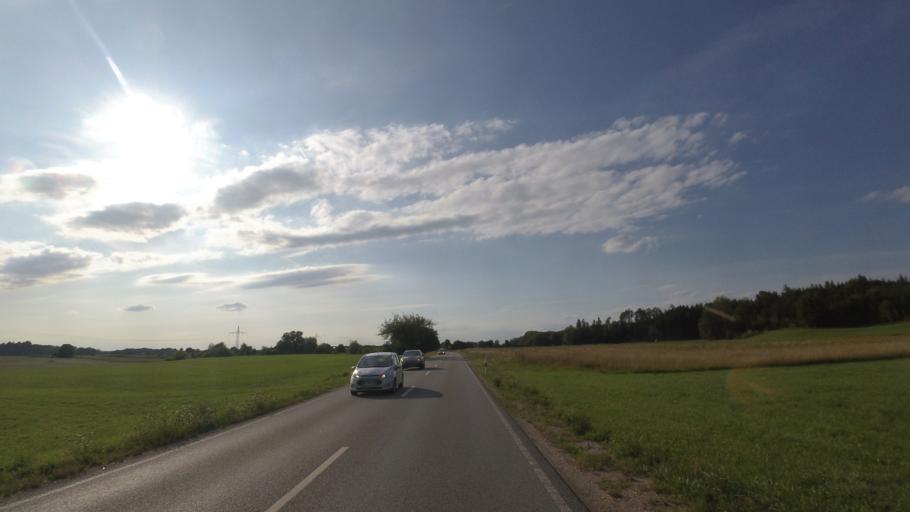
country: DE
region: Bavaria
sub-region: Upper Bavaria
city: Chieming
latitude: 47.9024
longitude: 12.5468
